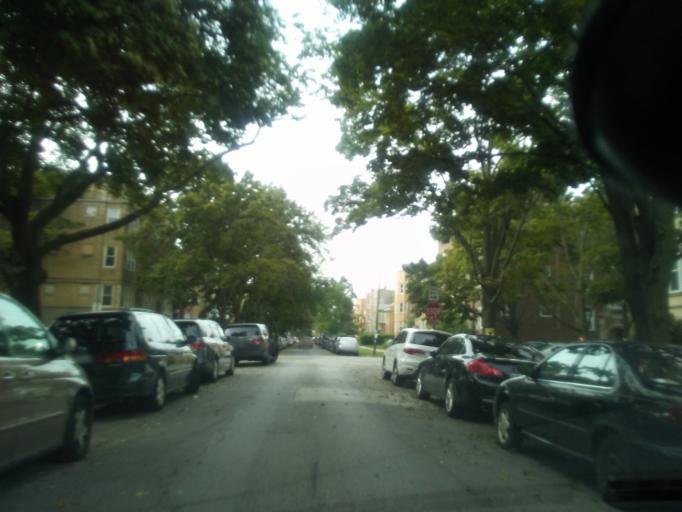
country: US
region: Illinois
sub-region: Cook County
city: Lincolnwood
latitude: 41.9998
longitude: -87.6973
